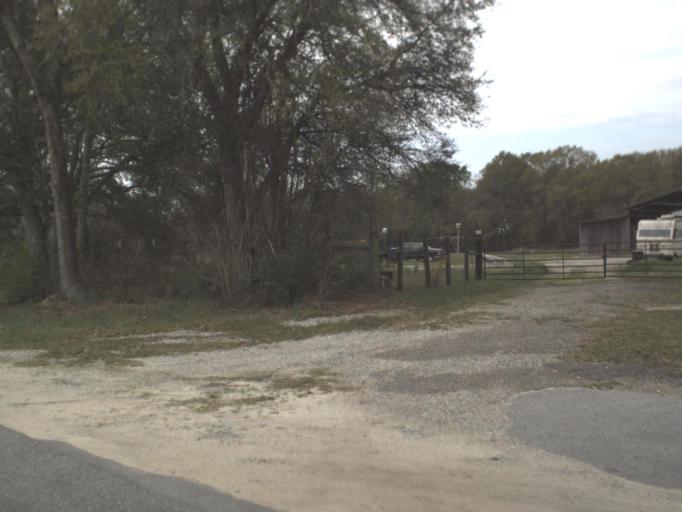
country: US
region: Florida
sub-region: Jackson County
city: Graceville
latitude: 30.9646
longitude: -85.6468
